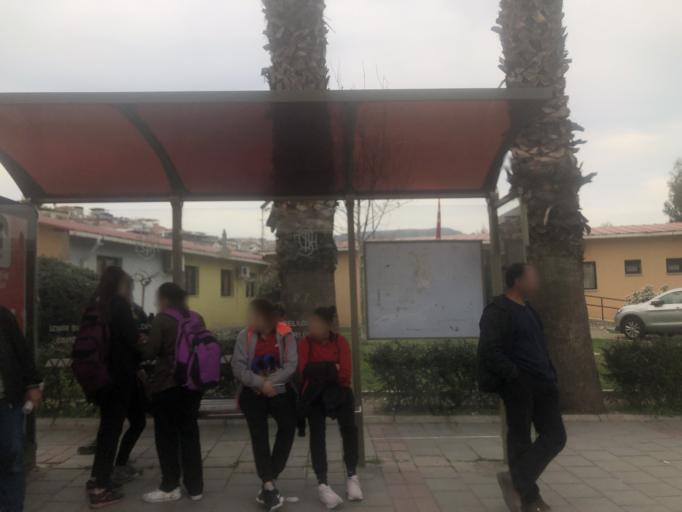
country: TR
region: Izmir
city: Karsiyaka
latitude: 38.4899
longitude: 27.0689
